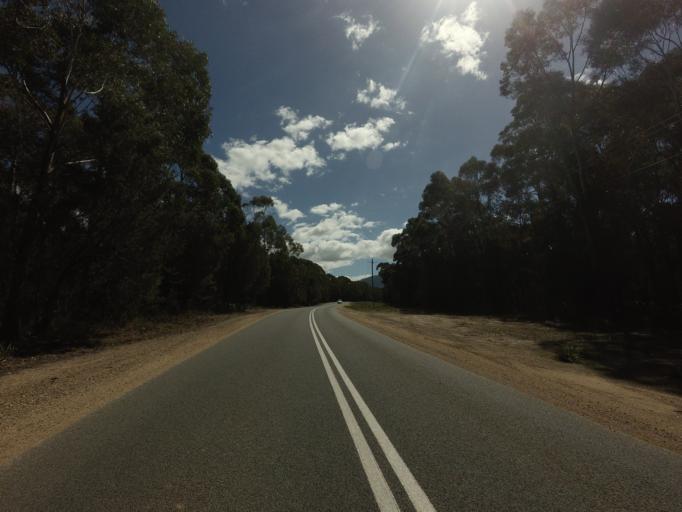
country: AU
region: Tasmania
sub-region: Break O'Day
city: St Helens
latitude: -41.6818
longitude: 148.2804
